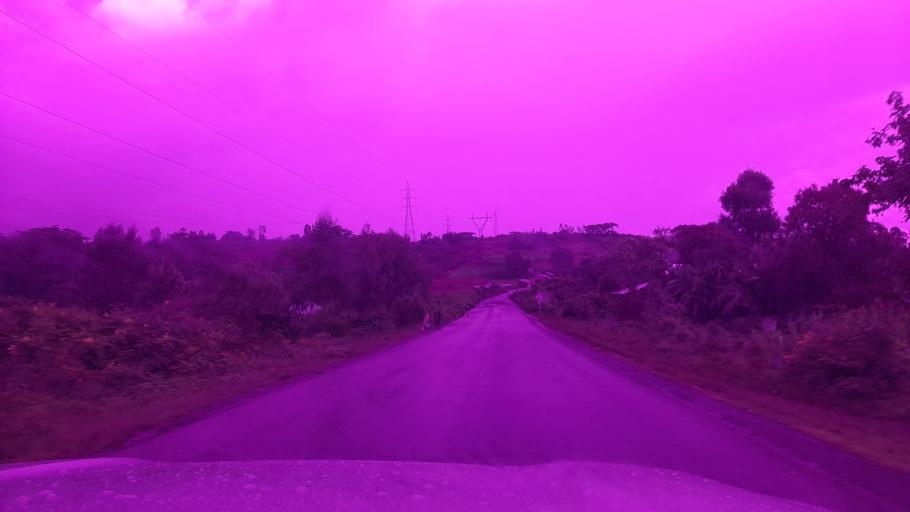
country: ET
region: Oromiya
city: Jima
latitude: 7.7137
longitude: 37.0852
